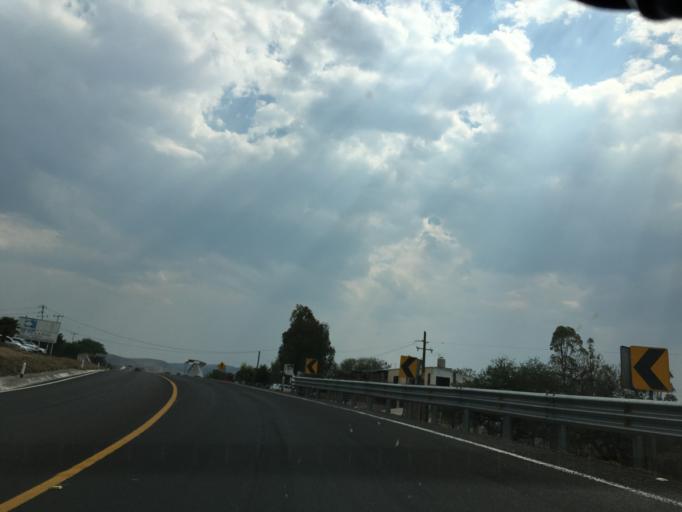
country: MX
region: Michoacan
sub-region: Cuitzeo
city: San Juan Benito Juarez (San Juan Tararameo)
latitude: 19.9243
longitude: -101.1415
